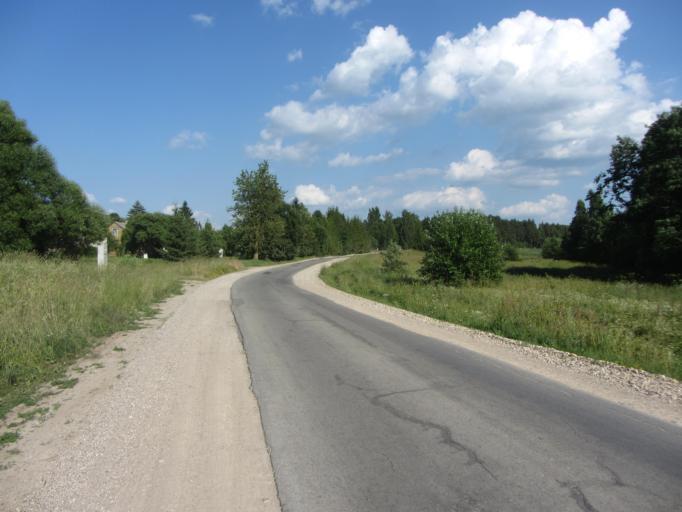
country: LT
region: Utenos apskritis
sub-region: Anyksciai
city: Anyksciai
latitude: 55.4495
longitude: 25.2258
